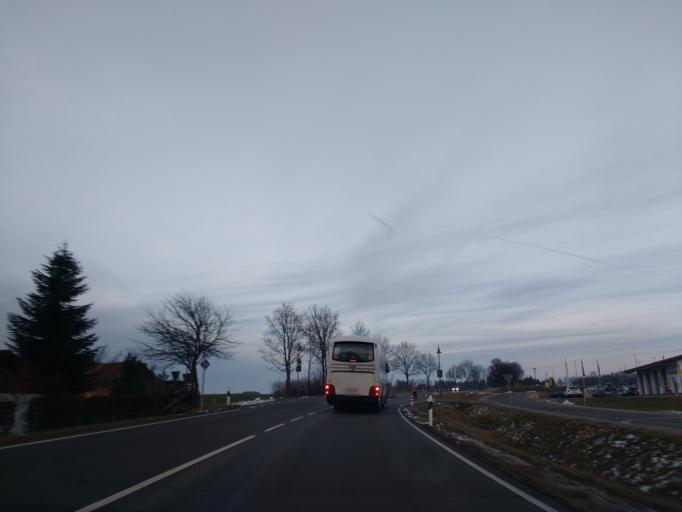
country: DE
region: Bavaria
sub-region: Swabia
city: Halblech
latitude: 47.6207
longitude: 10.8094
